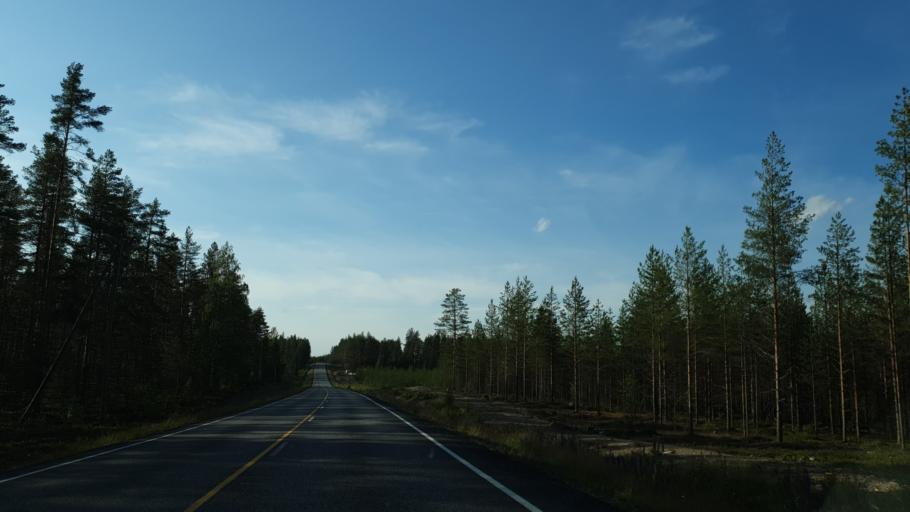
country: FI
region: Kainuu
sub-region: Kehys-Kainuu
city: Kuhmo
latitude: 64.0917
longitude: 29.4803
